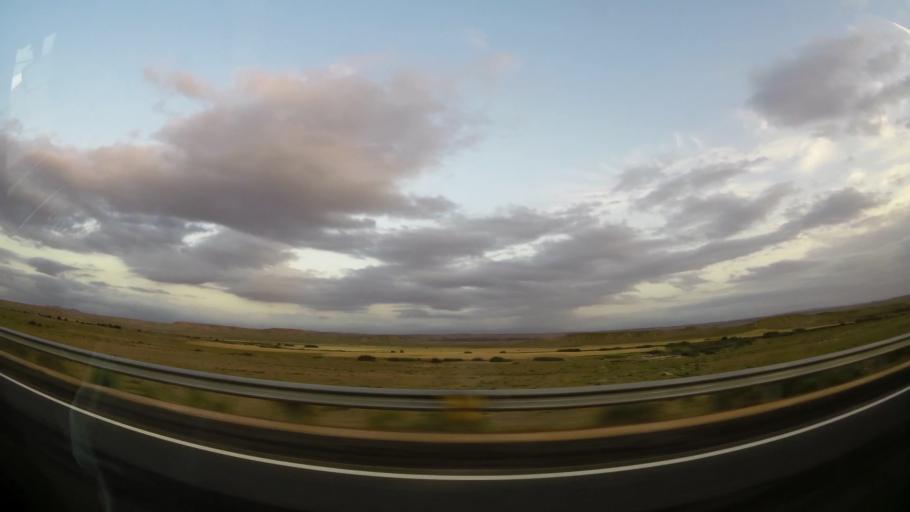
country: MA
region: Oriental
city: Taourirt
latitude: 34.5883
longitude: -2.7914
